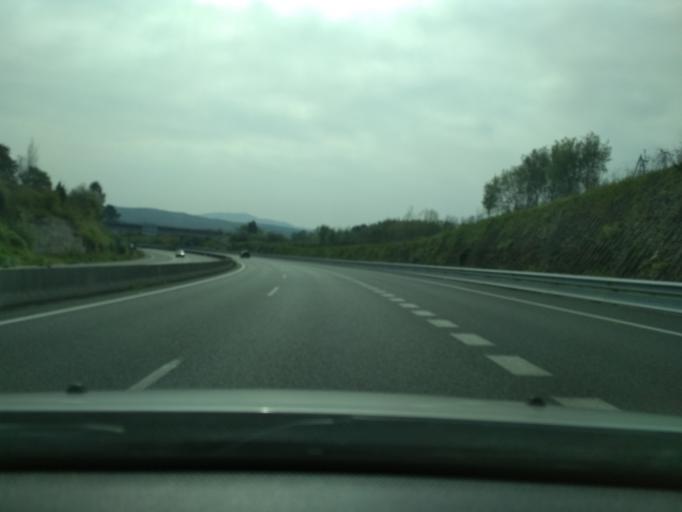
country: ES
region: Galicia
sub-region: Provincia da Coruna
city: Rianxo
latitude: 42.6692
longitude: -8.8263
